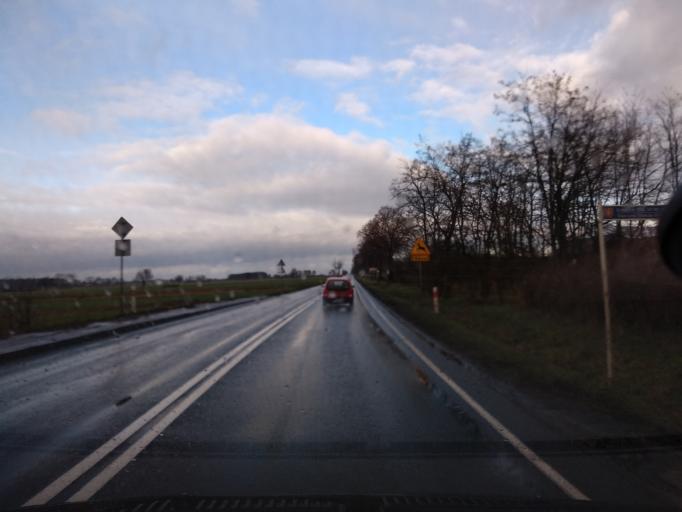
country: PL
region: Greater Poland Voivodeship
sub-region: Powiat koninski
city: Rychwal
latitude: 52.0409
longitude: 18.1618
